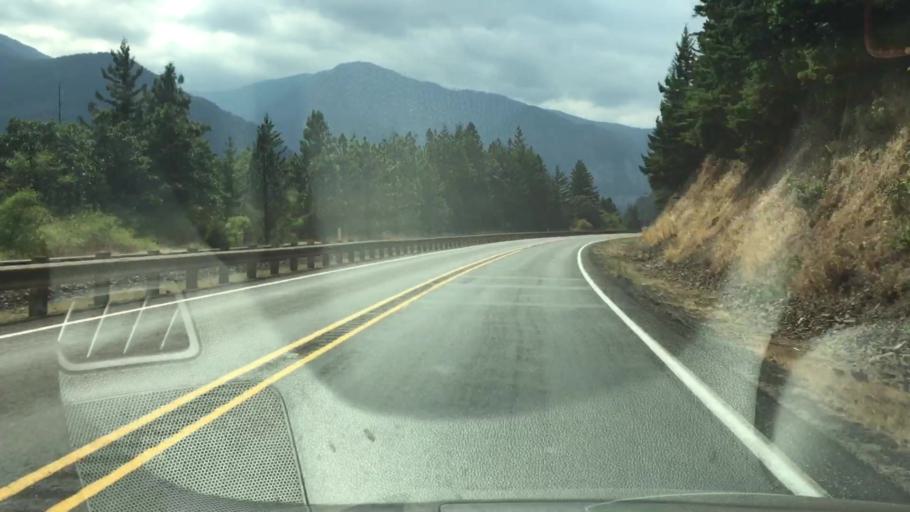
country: US
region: Washington
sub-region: Skamania County
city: Carson
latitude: 45.7055
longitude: -121.6848
